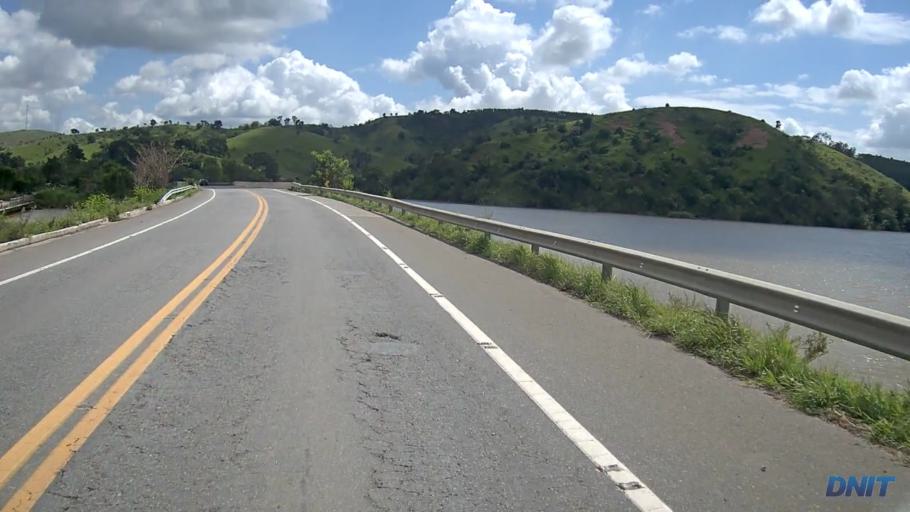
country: BR
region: Minas Gerais
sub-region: Governador Valadares
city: Governador Valadares
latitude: -19.0404
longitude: -42.1486
